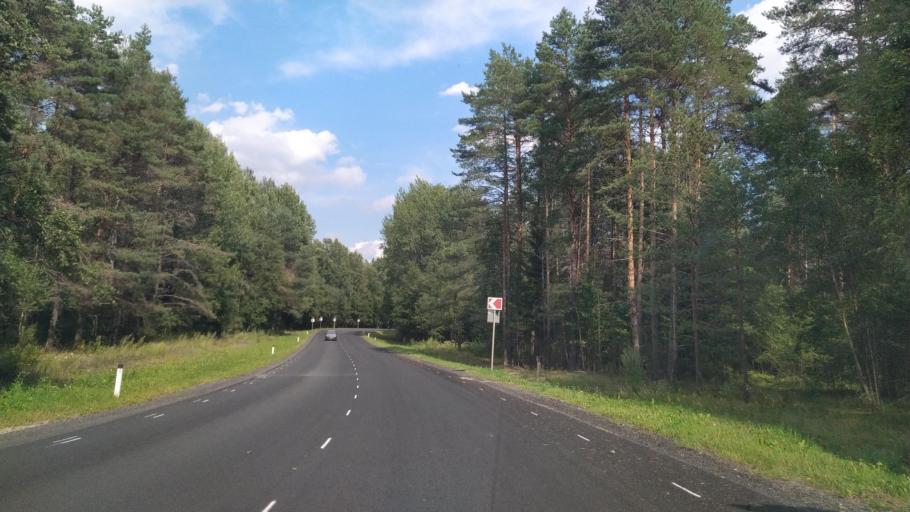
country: RU
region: Pskov
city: Porkhov
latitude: 57.7343
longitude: 29.4054
